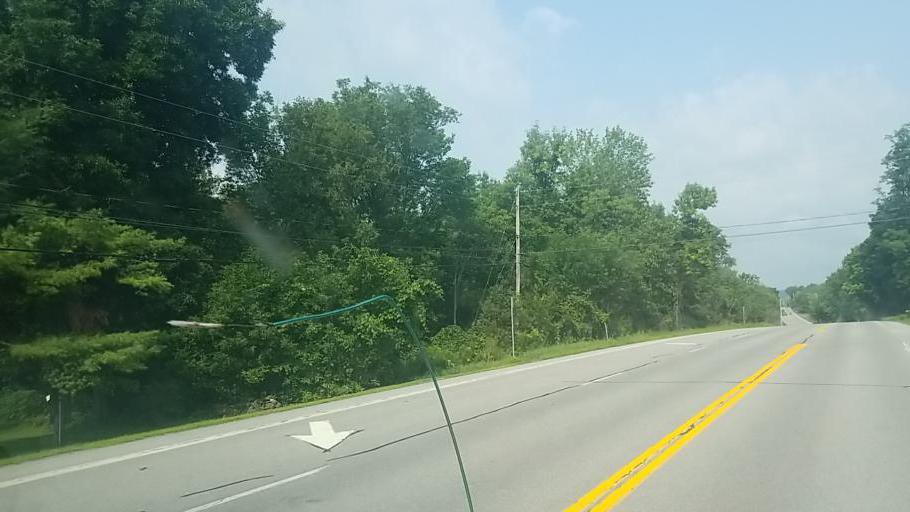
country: US
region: New York
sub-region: Montgomery County
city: Saint Johnsville
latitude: 42.9810
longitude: -74.6415
